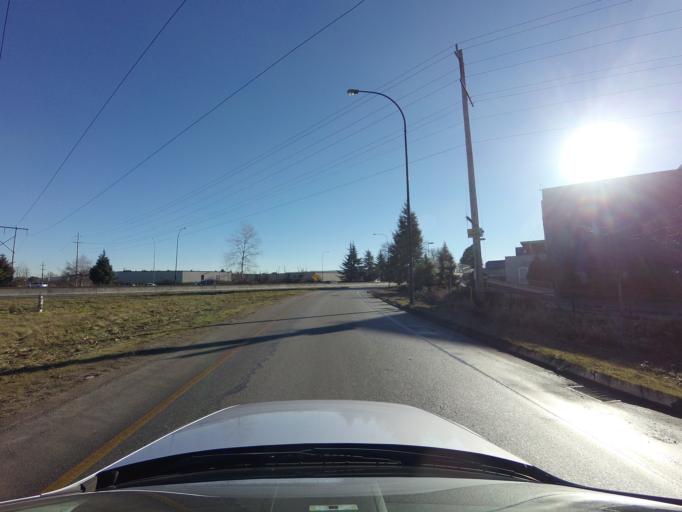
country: CA
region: British Columbia
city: Richmond
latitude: 49.1904
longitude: -123.0785
